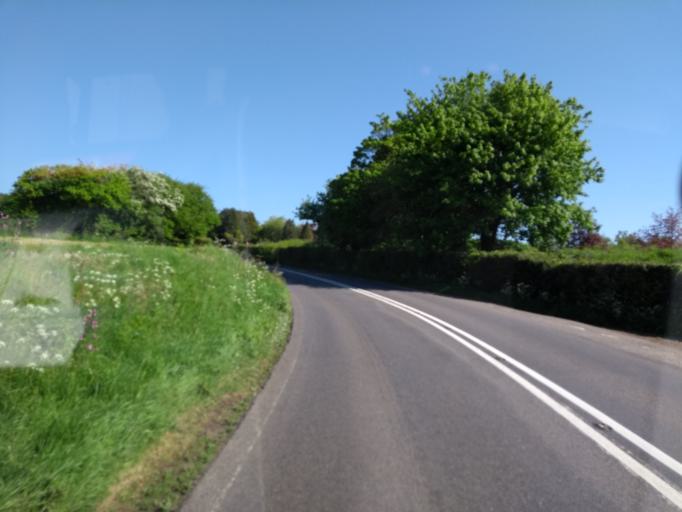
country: GB
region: England
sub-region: Devon
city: Axminster
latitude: 50.8228
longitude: -2.9692
